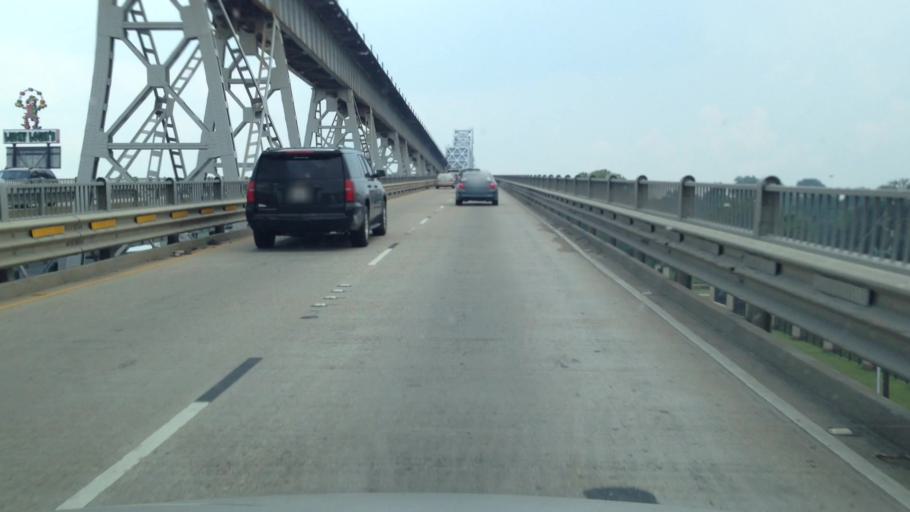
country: US
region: Louisiana
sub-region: West Baton Rouge Parish
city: Port Allen
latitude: 30.5063
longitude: -91.2078
